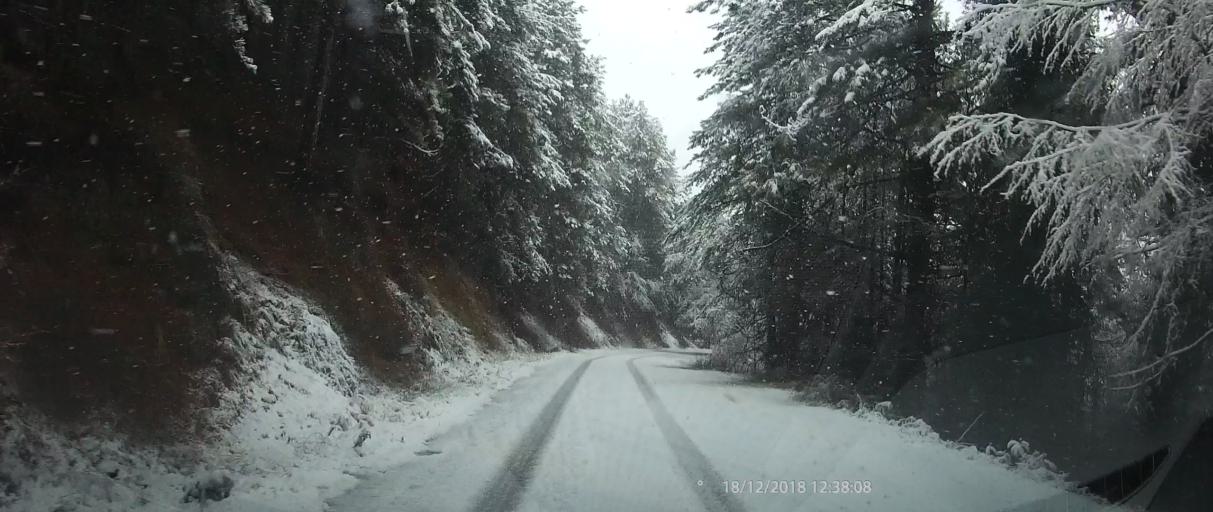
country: GR
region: Central Macedonia
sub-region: Nomos Pierias
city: Litochoro
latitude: 40.0894
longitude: 22.4130
